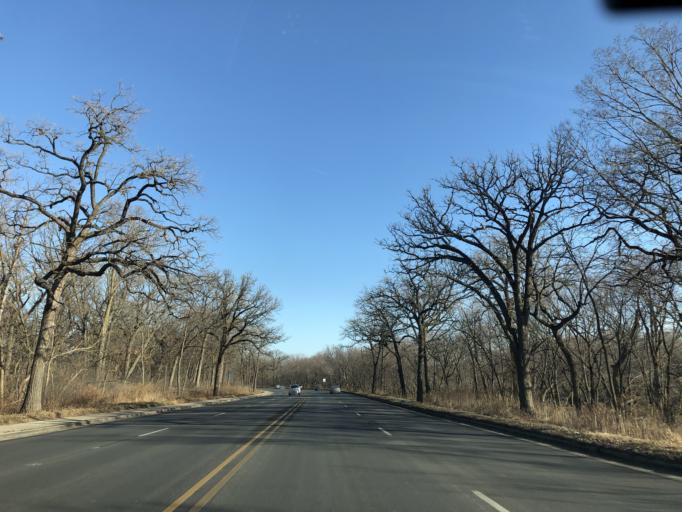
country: US
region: Illinois
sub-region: Cook County
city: Lyons
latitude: 41.8207
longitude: -87.8316
